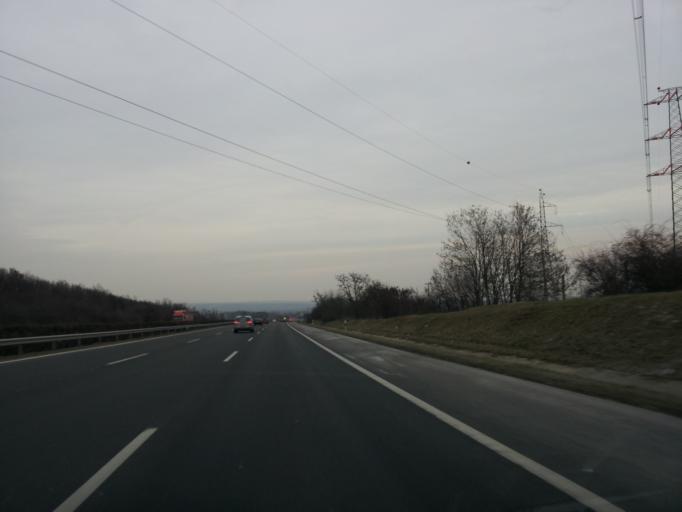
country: HU
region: Fejer
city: Martonvasar
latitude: 47.3535
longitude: 18.8053
